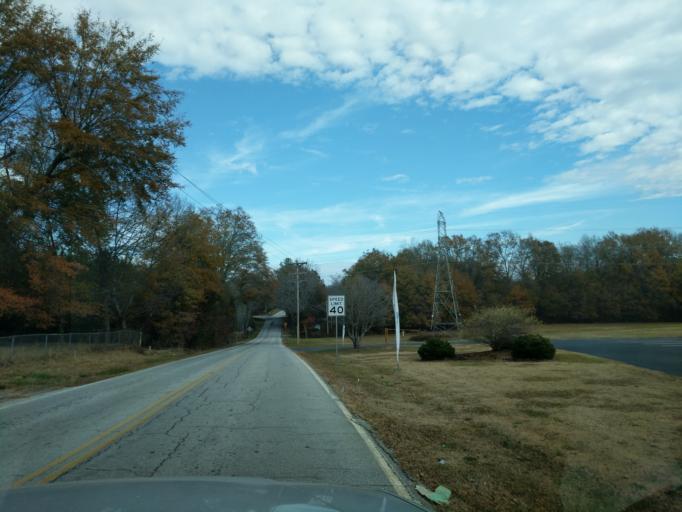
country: US
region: South Carolina
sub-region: Pickens County
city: Arial
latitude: 34.8526
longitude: -82.6458
